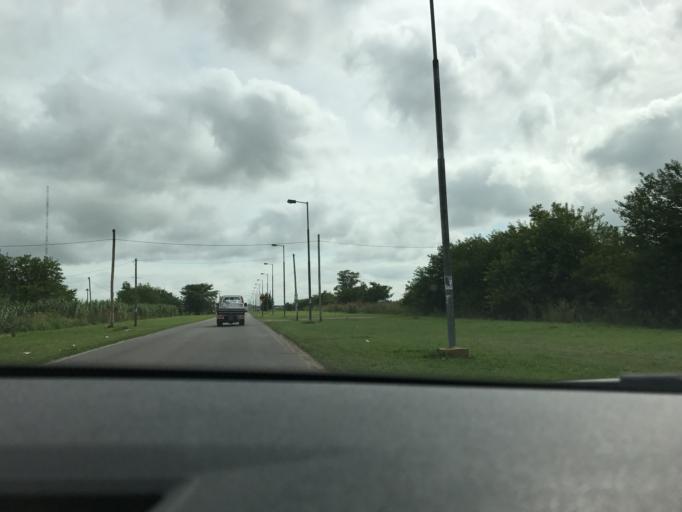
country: AR
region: Buenos Aires
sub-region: Partido de La Plata
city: La Plata
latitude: -34.8454
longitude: -58.0762
